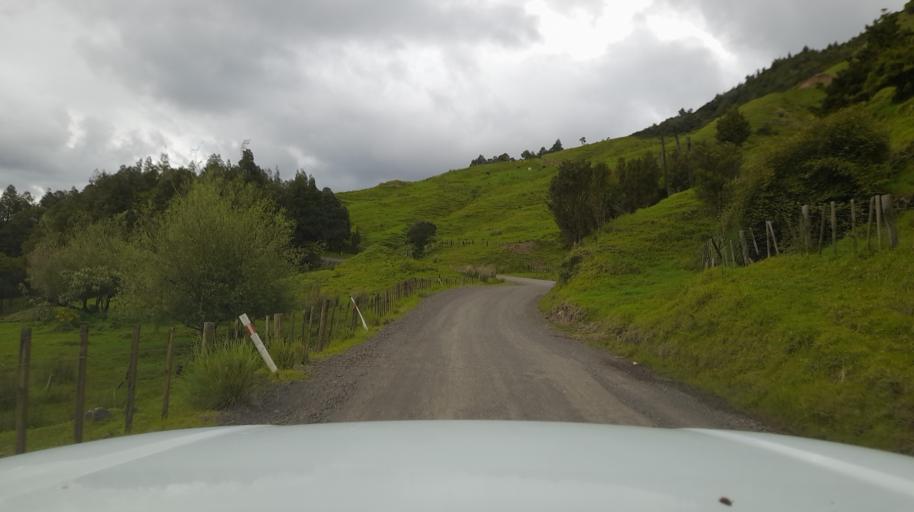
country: NZ
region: Northland
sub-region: Far North District
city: Kaitaia
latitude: -35.3419
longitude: 173.3615
